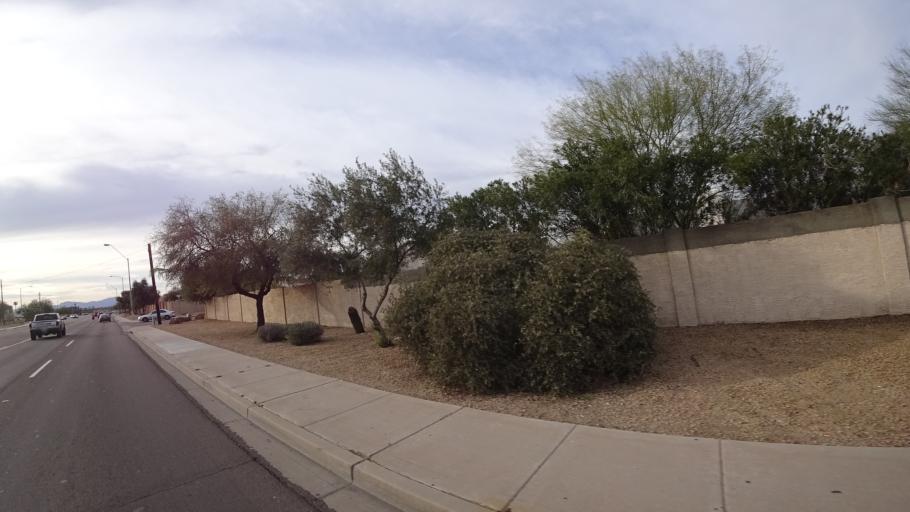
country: US
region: Arizona
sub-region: Maricopa County
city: Peoria
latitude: 33.5664
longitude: -112.2501
